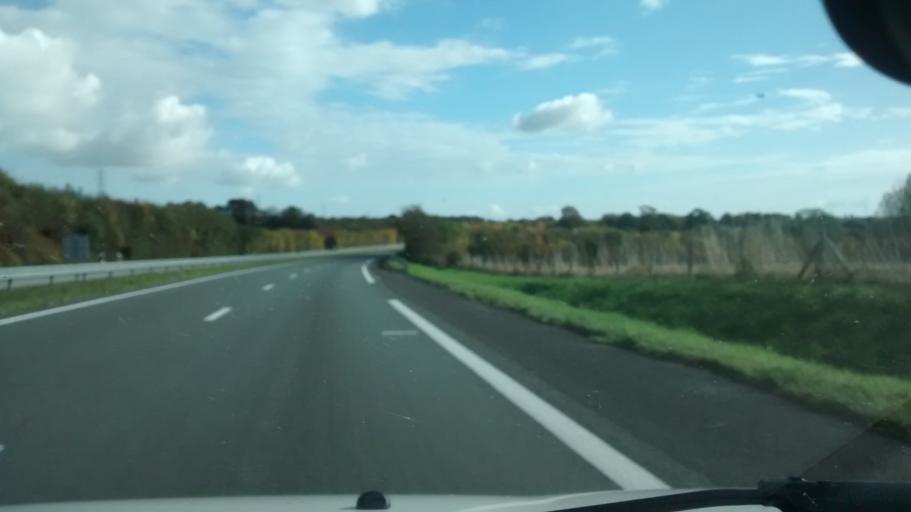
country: FR
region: Pays de la Loire
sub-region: Departement de Maine-et-Loire
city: Pouance
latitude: 47.7603
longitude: -1.1988
